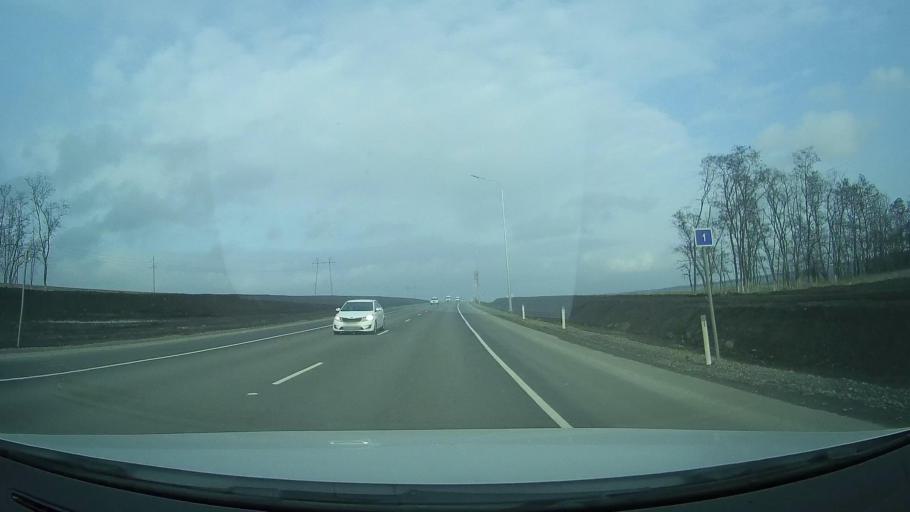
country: RU
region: Rostov
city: Grushevskaya
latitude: 47.3870
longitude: 39.8461
